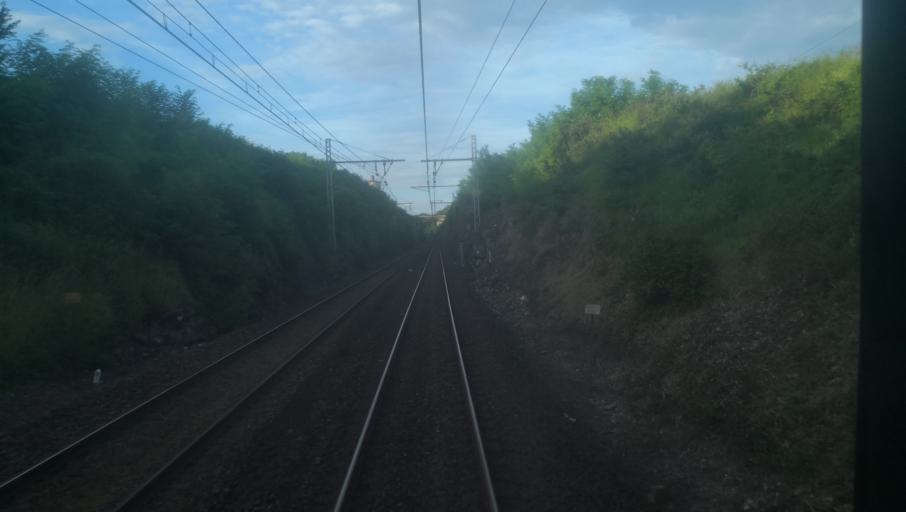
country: FR
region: Centre
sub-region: Departement de l'Indre
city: Saint-Marcel
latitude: 46.6217
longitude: 1.5010
